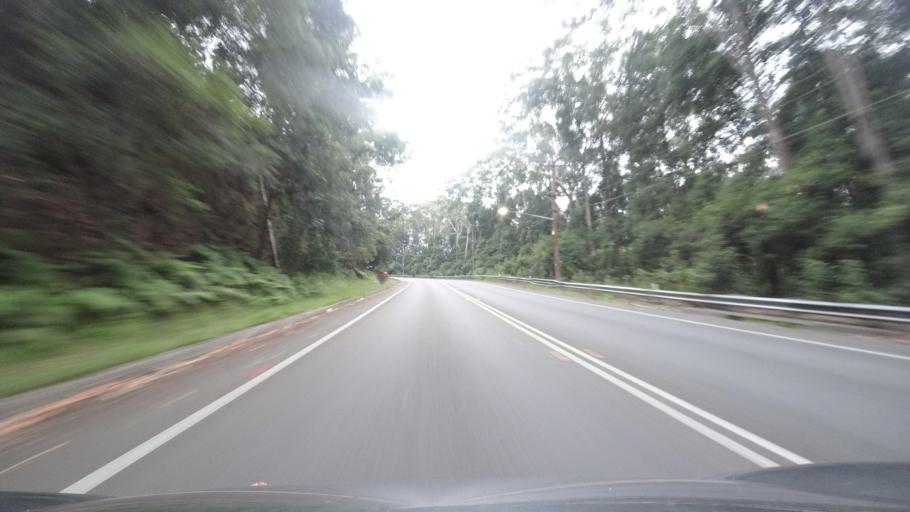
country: AU
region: New South Wales
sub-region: Ku-ring-gai
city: Normanhurst
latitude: -33.7385
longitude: 151.1065
